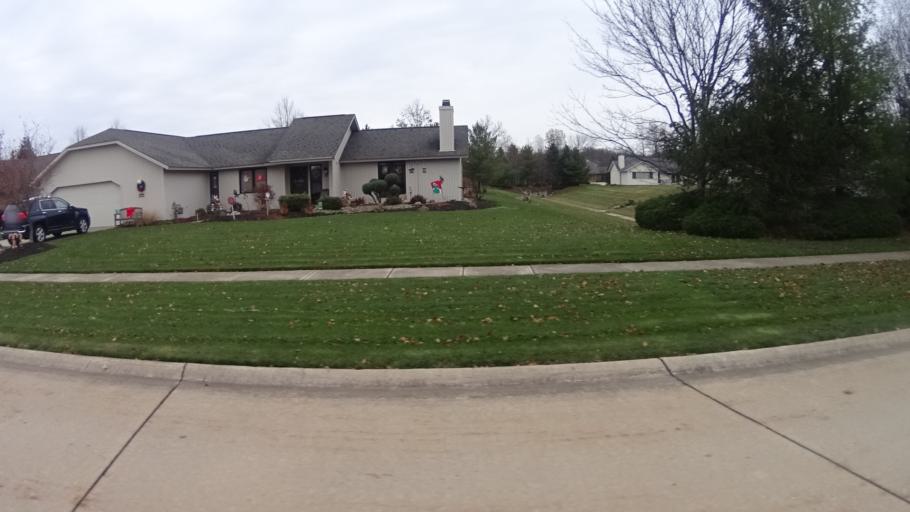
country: US
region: Ohio
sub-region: Lorain County
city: North Ridgeville
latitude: 41.3670
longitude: -81.9795
